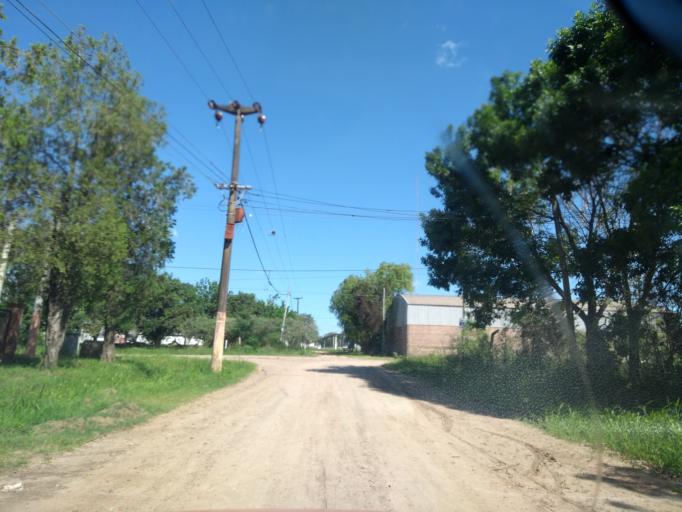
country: AR
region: Chaco
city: Resistencia
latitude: -27.4252
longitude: -58.9439
